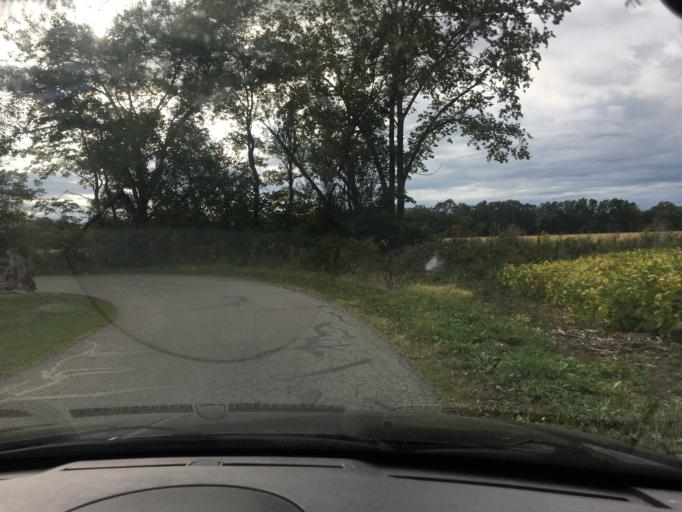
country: US
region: Ohio
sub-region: Logan County
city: West Liberty
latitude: 40.2575
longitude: -83.7442
